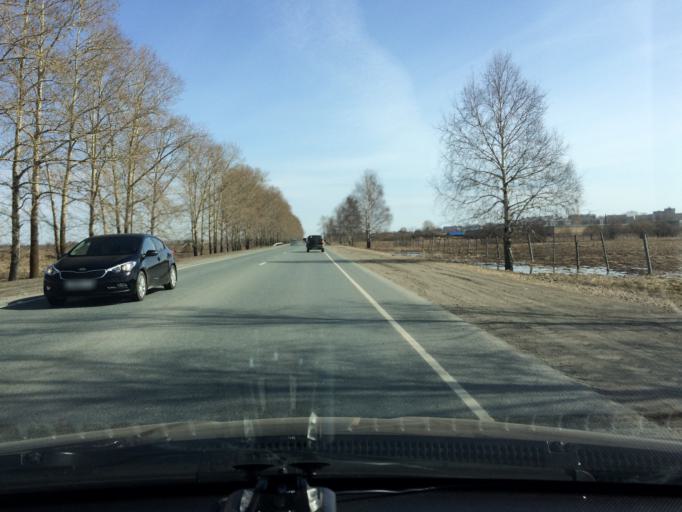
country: RU
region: Mariy-El
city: Yoshkar-Ola
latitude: 56.6498
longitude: 47.9452
